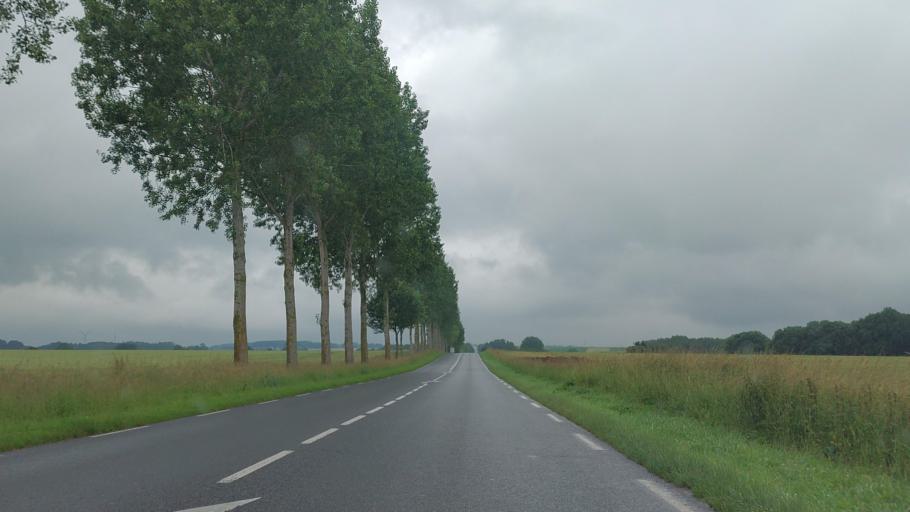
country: FR
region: Picardie
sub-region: Departement de la Somme
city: Chepy
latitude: 50.0898
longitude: 1.6876
